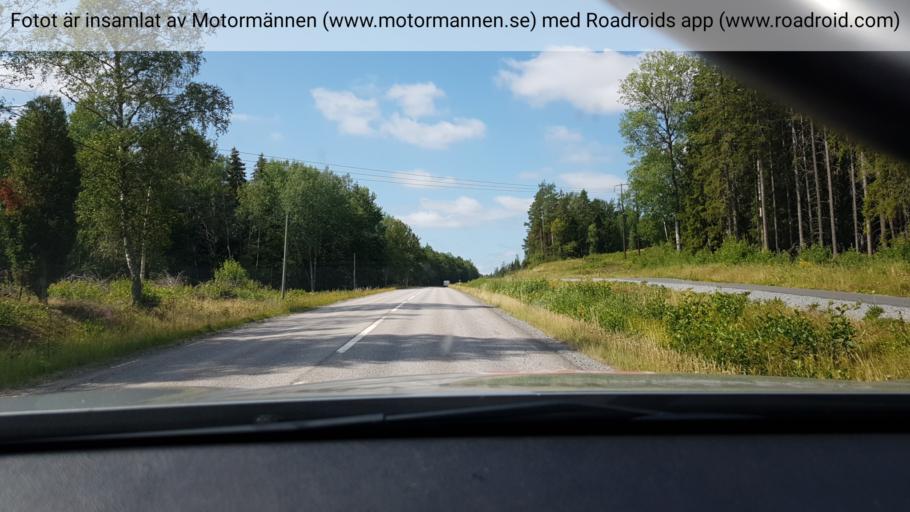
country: SE
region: Stockholm
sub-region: Vallentuna Kommun
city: Vallentuna
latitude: 59.5341
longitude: 18.1290
